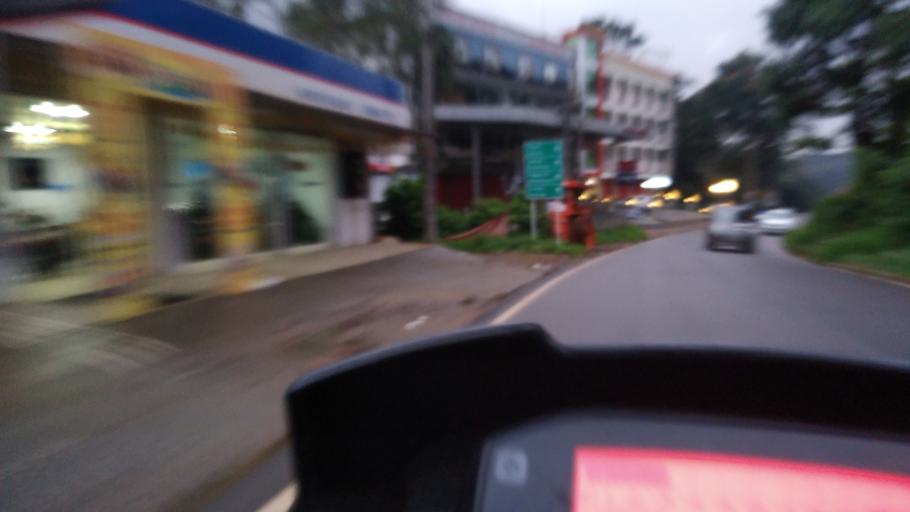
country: IN
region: Kerala
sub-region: Idukki
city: Munnar
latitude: 9.9605
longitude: 77.0970
